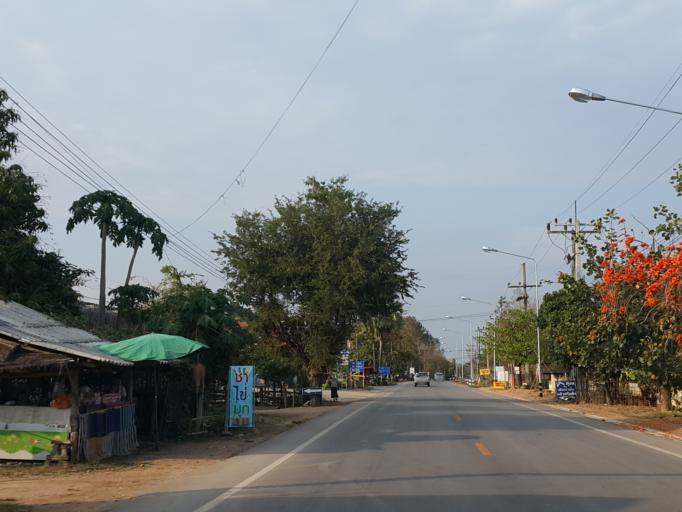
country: TH
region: Lampang
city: Chae Hom
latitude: 18.5321
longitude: 99.4781
